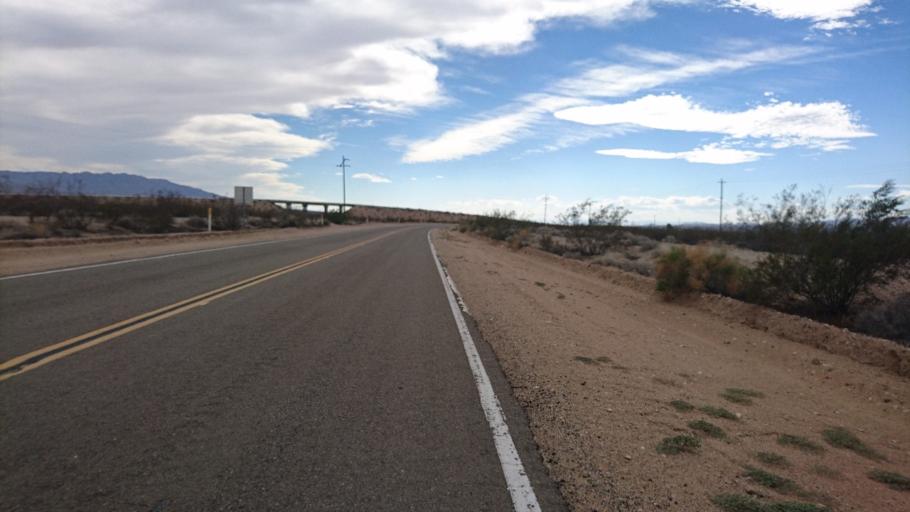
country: US
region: California
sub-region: San Bernardino County
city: Needles
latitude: 34.7567
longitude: -115.2192
